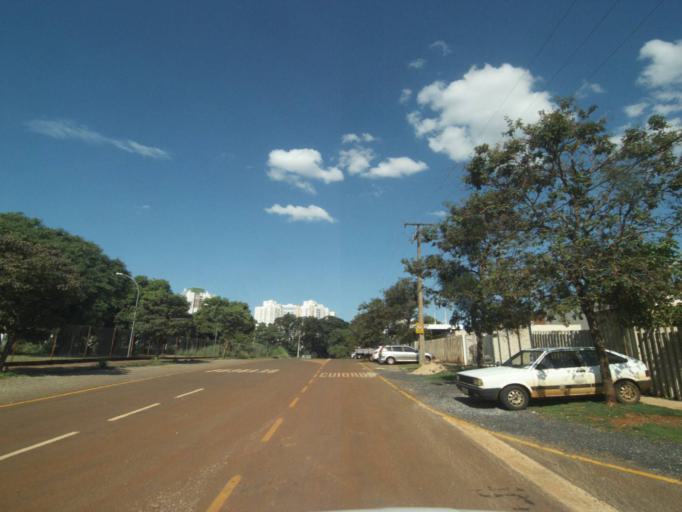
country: BR
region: Parana
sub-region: Londrina
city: Londrina
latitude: -23.3351
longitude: -51.1874
